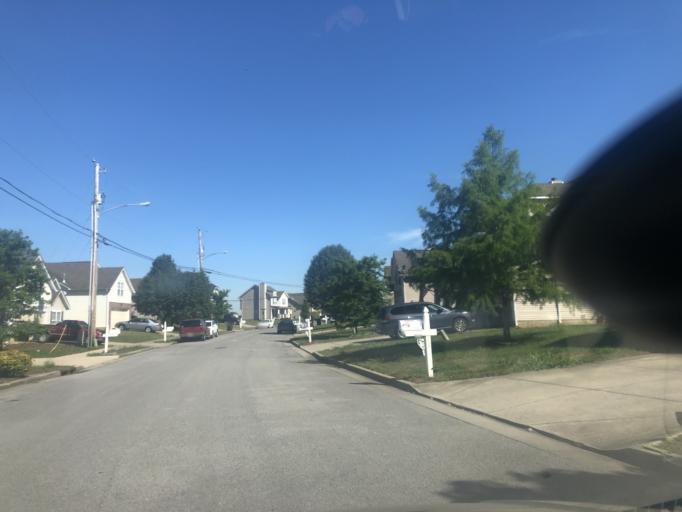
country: US
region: Tennessee
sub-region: Davidson County
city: Lakewood
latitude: 36.2430
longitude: -86.6636
